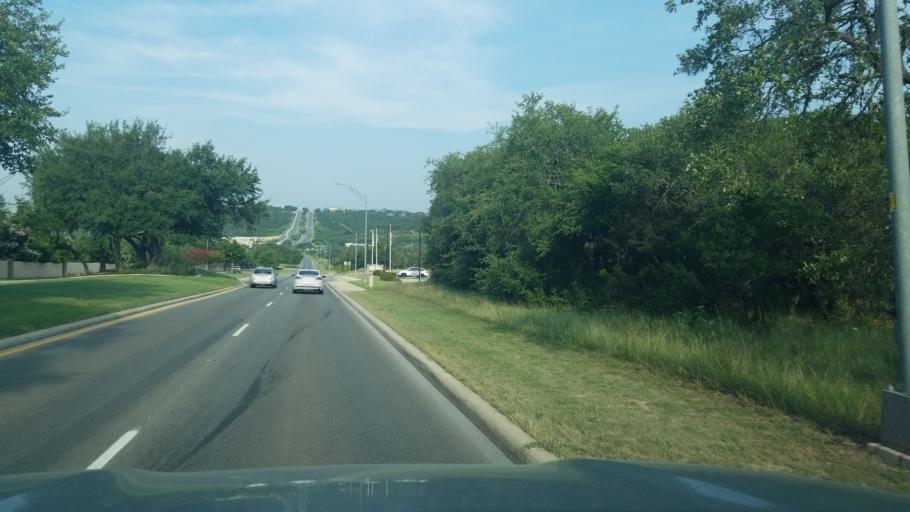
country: US
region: Texas
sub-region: Bexar County
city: Hollywood Park
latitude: 29.6443
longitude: -98.4739
